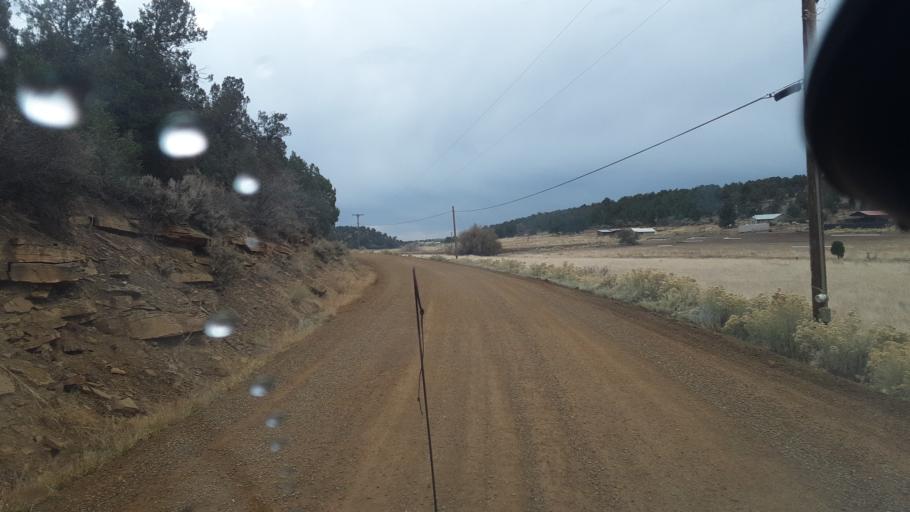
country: US
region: Colorado
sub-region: Montezuma County
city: Mancos
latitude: 37.2039
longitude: -108.1389
